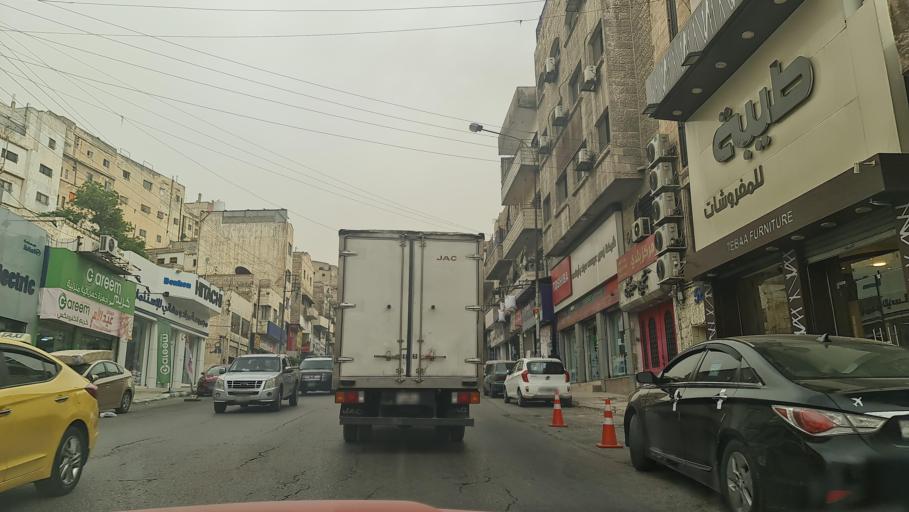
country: JO
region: Amman
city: Amman
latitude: 31.9413
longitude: 35.9292
